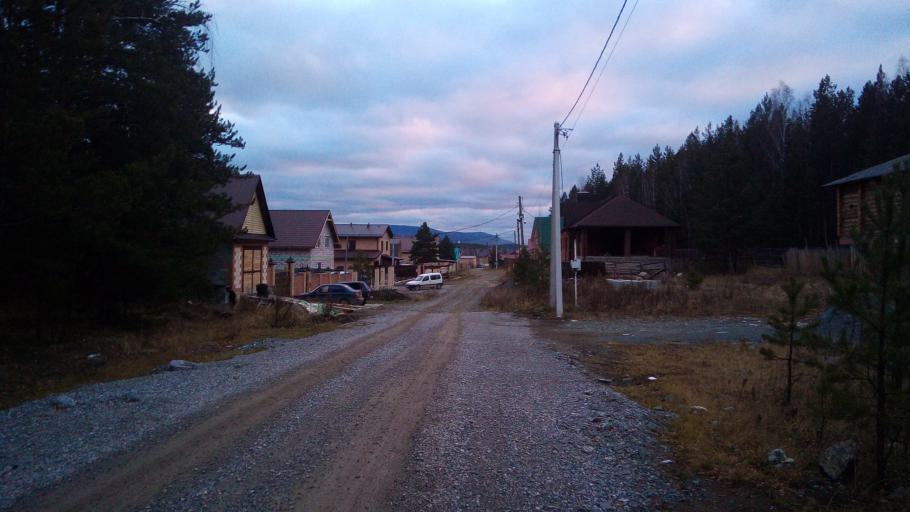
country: RU
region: Chelyabinsk
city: Turgoyak
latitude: 55.1779
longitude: 60.1312
